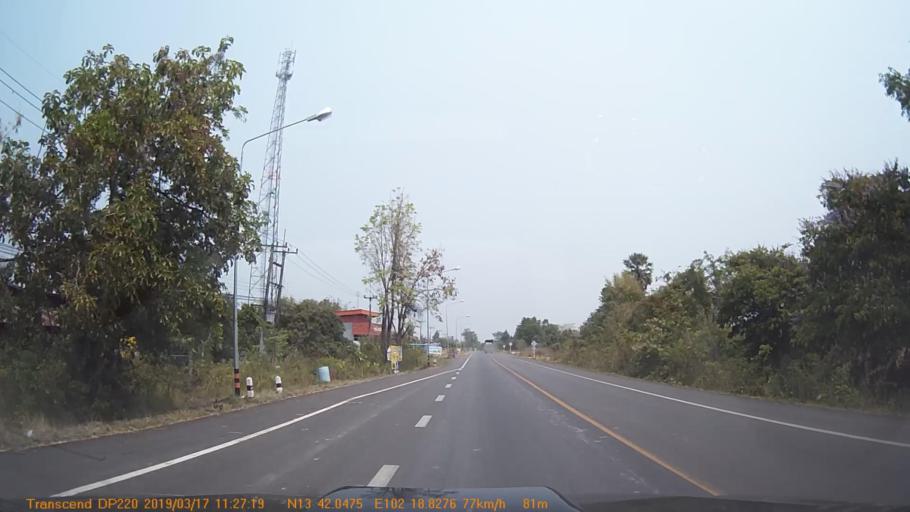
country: TH
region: Sa Kaeo
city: Watthana Nakhon
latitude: 13.7010
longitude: 102.3138
